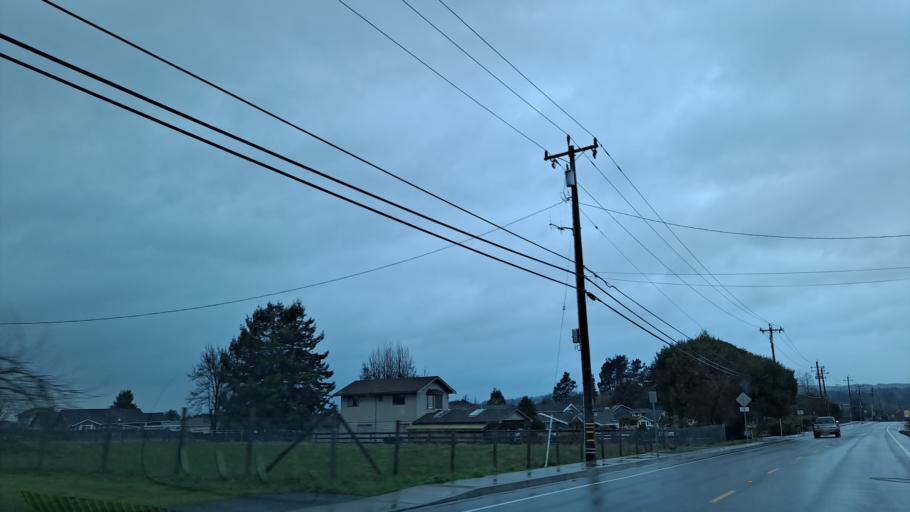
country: US
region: California
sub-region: Humboldt County
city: Fortuna
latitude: 40.5769
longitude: -124.1292
